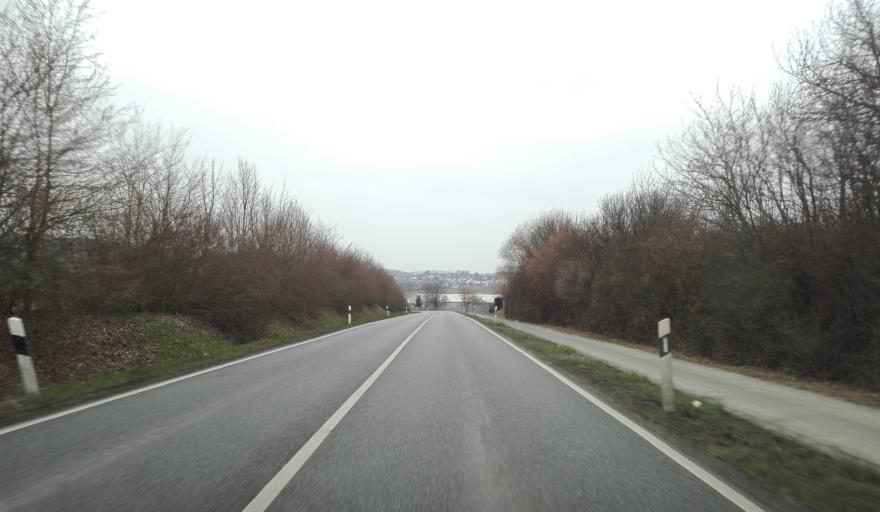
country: DE
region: Hesse
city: Ober-Ramstadt
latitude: 49.8189
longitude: 8.7620
